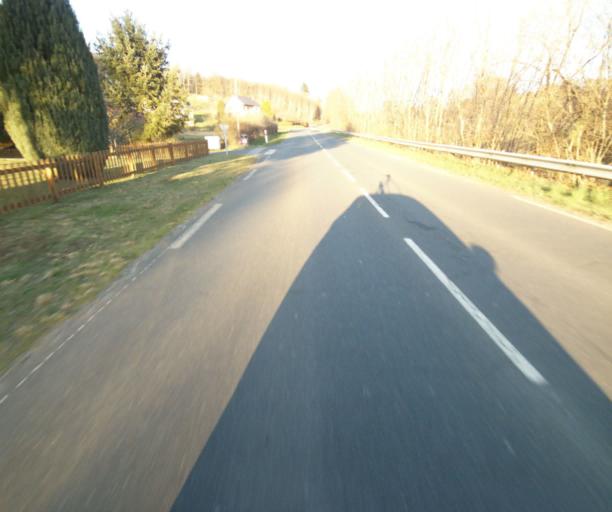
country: FR
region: Limousin
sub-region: Departement de la Correze
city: Saint-Clement
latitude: 45.3456
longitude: 1.6892
